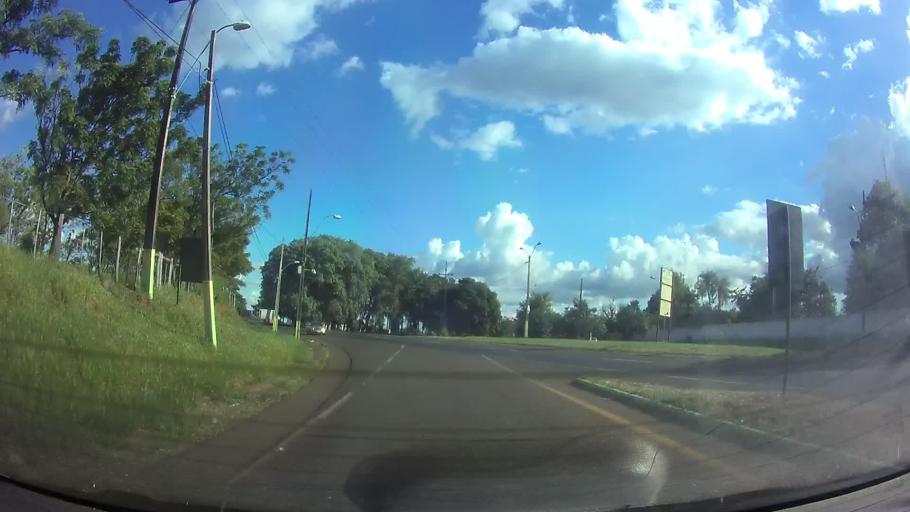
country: PY
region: Cordillera
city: Caacupe
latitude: -25.3863
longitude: -57.1967
